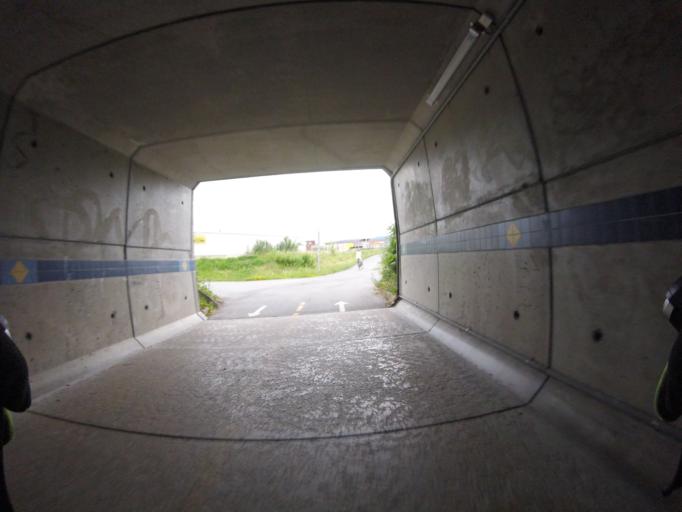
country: NO
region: Akershus
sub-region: Skedsmo
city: Lillestrom
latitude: 59.9783
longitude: 11.0010
